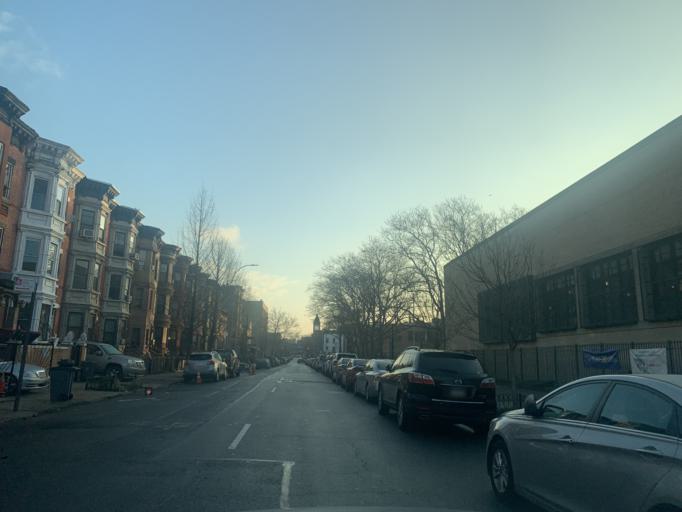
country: US
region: New York
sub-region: Kings County
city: Brooklyn
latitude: 40.6920
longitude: -73.9333
